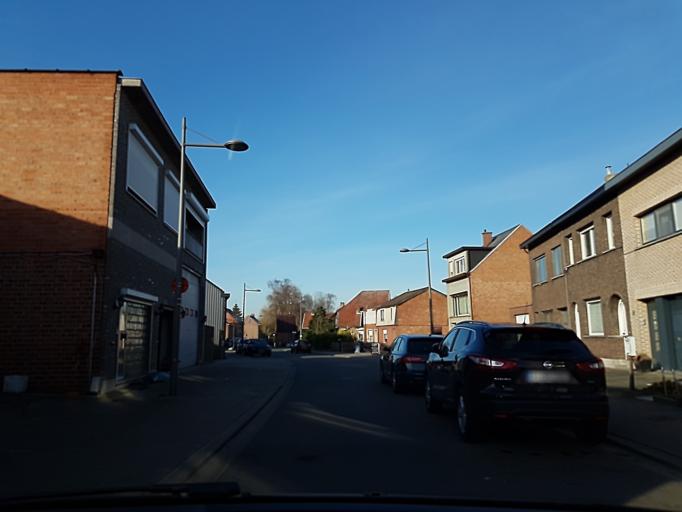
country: BE
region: Flanders
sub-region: Provincie Antwerpen
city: Niel
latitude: 51.0899
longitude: 4.3312
